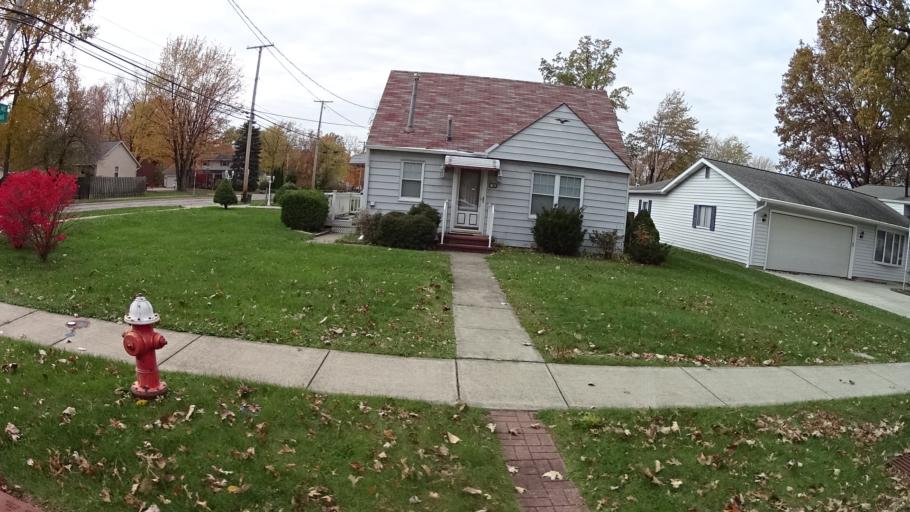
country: US
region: Ohio
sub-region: Lorain County
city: Sheffield Lake
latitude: 41.4852
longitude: -82.0994
